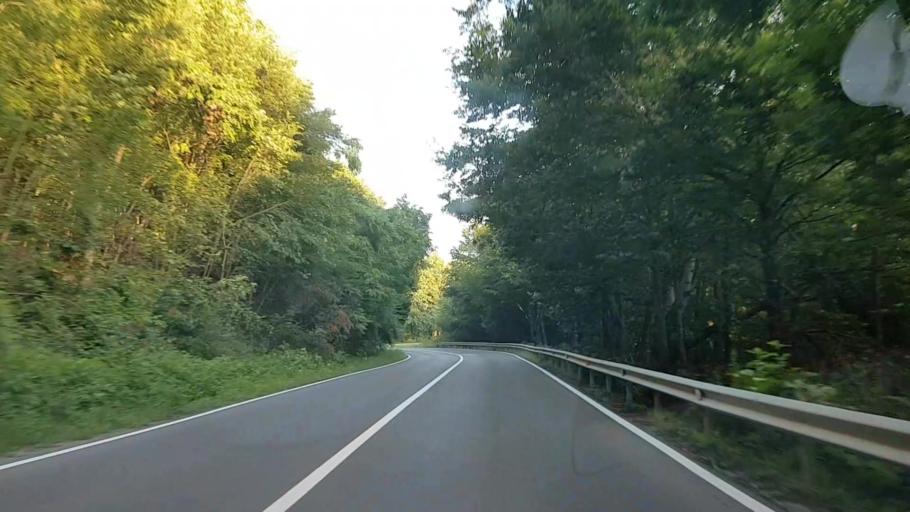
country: RO
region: Harghita
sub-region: Comuna Lupeni
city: Lupeni
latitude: 46.4365
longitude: 25.2313
